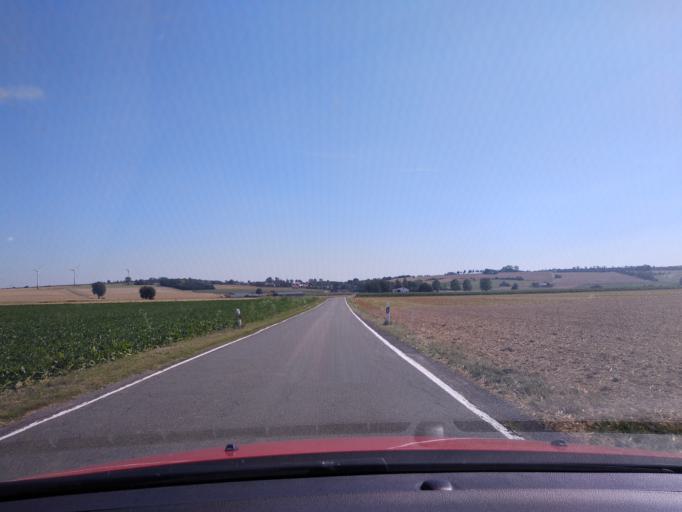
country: DE
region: North Rhine-Westphalia
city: Brakel
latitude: 51.6499
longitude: 9.1677
